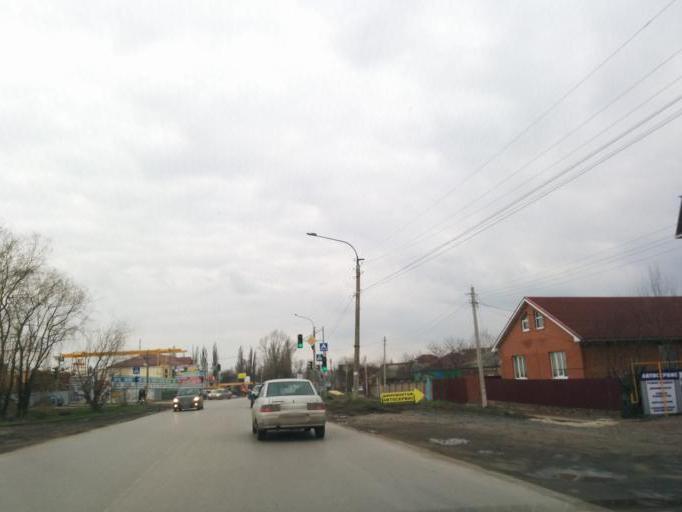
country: RU
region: Rostov
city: Novocherkassk
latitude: 47.4555
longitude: 40.1024
